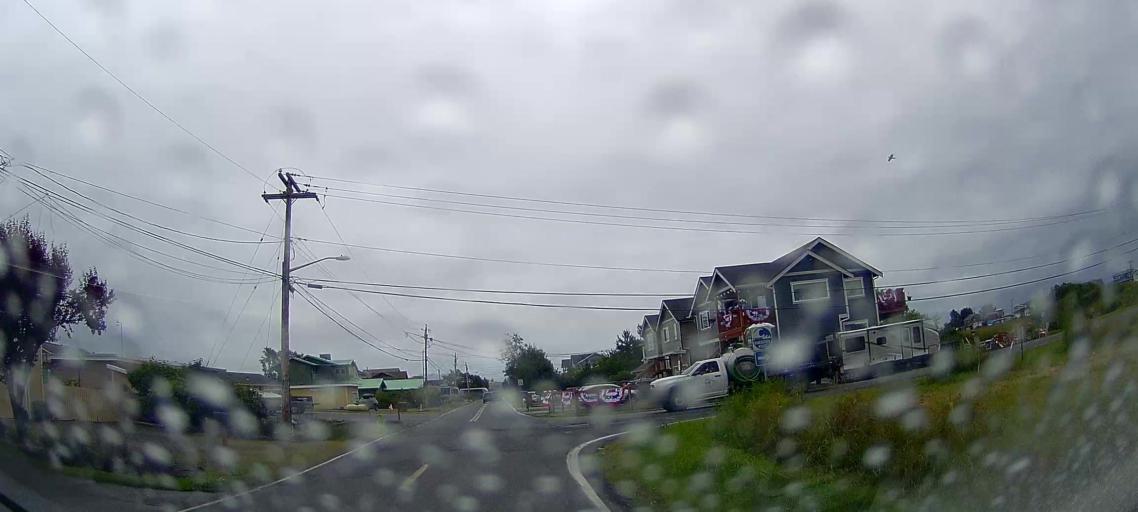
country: US
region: Washington
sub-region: Whatcom County
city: Birch Bay
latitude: 48.8020
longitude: -122.7075
